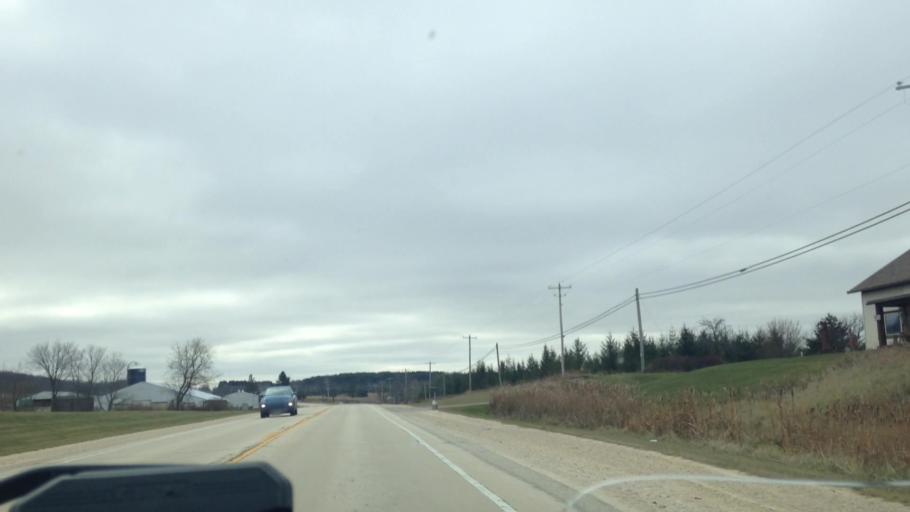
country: US
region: Wisconsin
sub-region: Dodge County
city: Mayville
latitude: 43.4701
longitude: -88.5464
